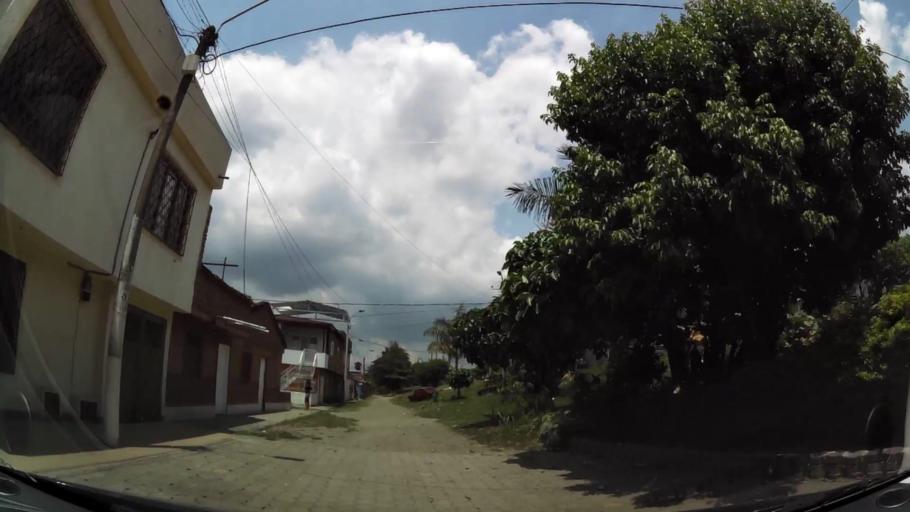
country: CO
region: Valle del Cauca
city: Cali
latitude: 3.4562
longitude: -76.4776
